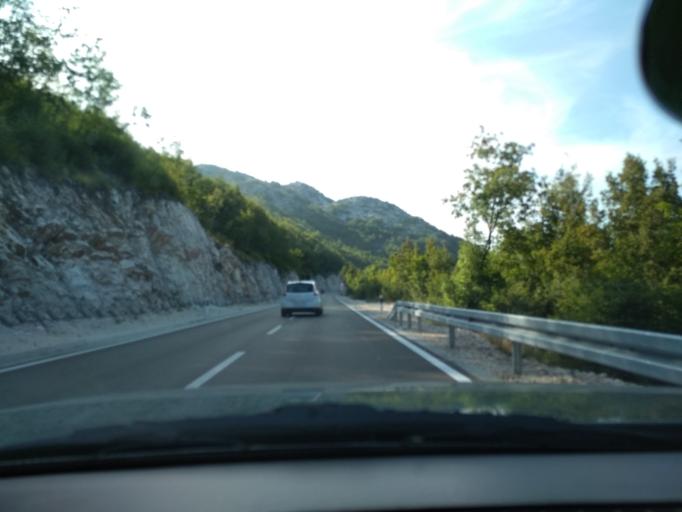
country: ME
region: Cetinje
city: Cetinje
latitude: 42.4176
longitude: 18.8779
